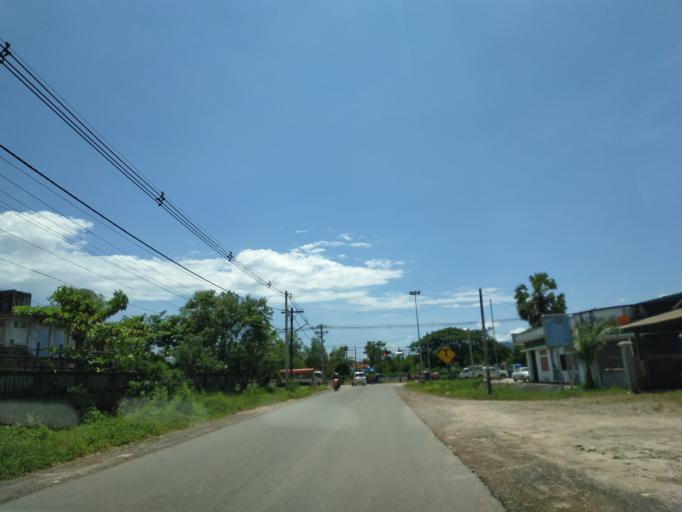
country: MM
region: Tanintharyi
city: Dawei
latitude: 14.0917
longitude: 98.1841
